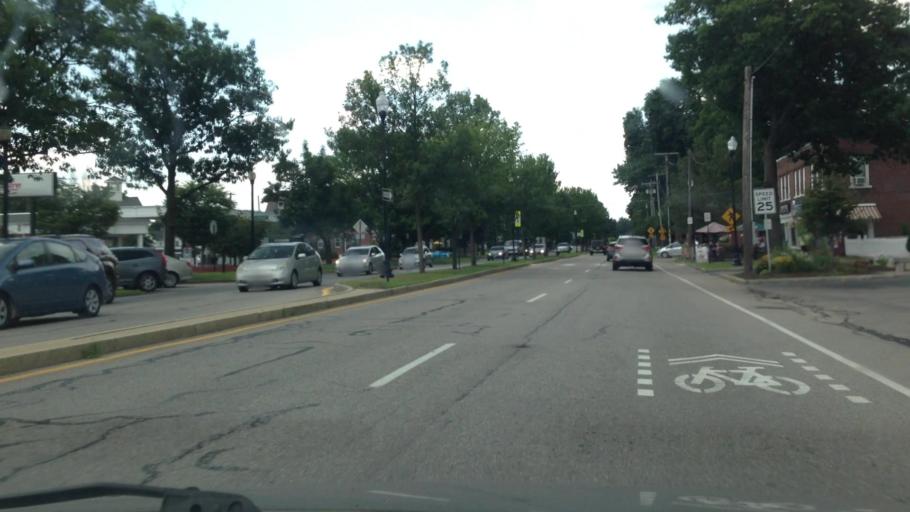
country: US
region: New Hampshire
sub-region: Cheshire County
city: Keene
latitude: 42.9309
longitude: -72.2781
